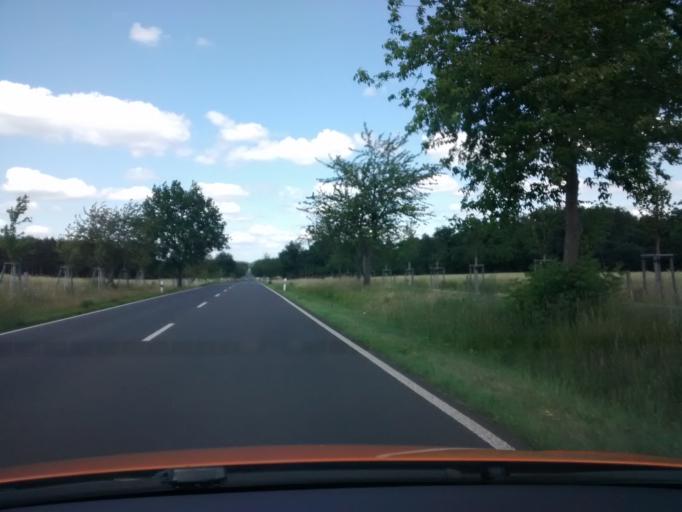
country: DE
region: Berlin
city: Kladow
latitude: 52.4811
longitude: 13.1087
